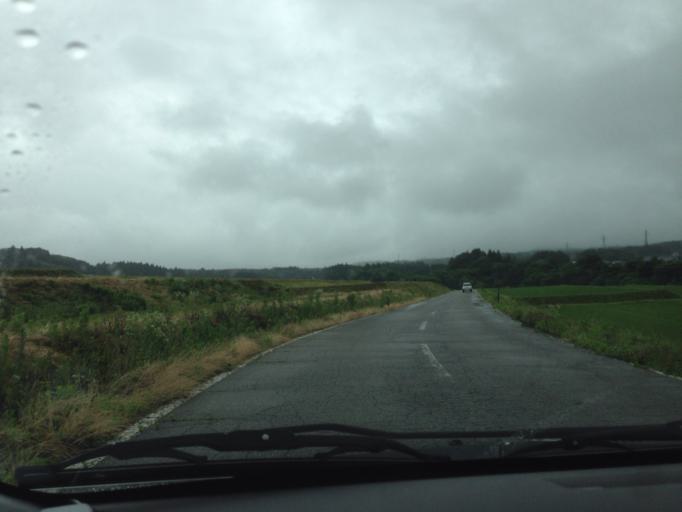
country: JP
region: Fukushima
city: Inawashiro
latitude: 37.5657
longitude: 139.9928
